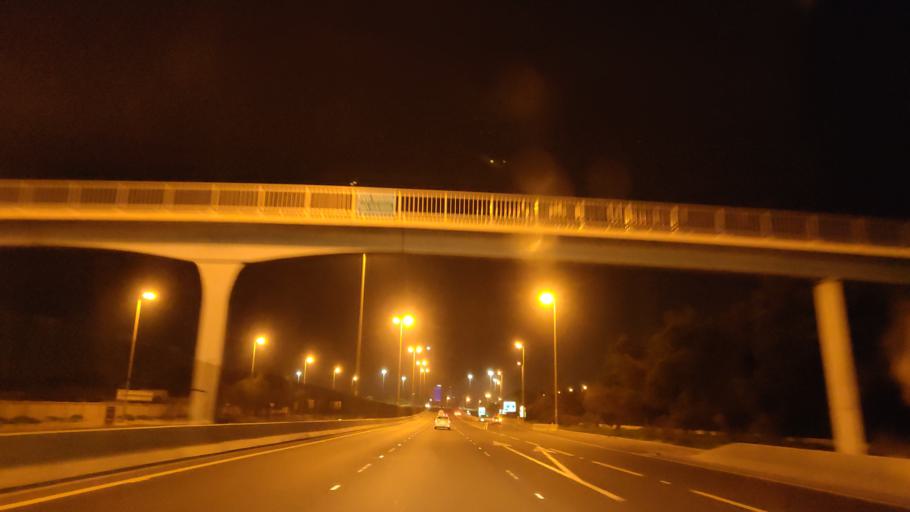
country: KW
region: Al Asimah
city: Ash Shamiyah
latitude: 29.3275
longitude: 47.9724
